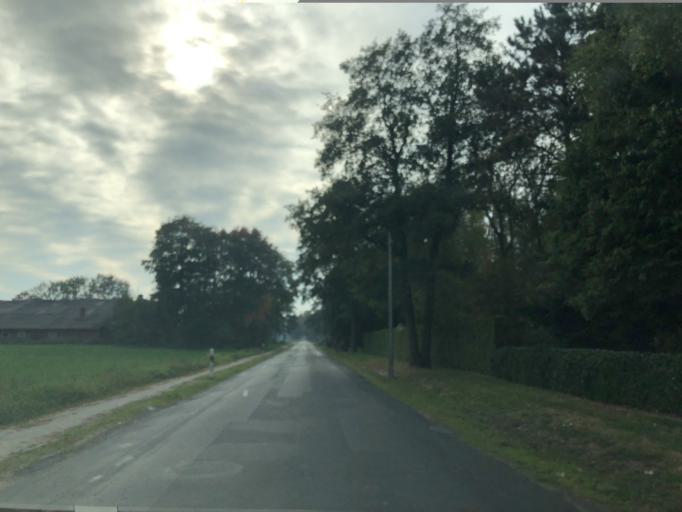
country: DE
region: Lower Saxony
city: Papenburg
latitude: 53.0559
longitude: 7.3897
